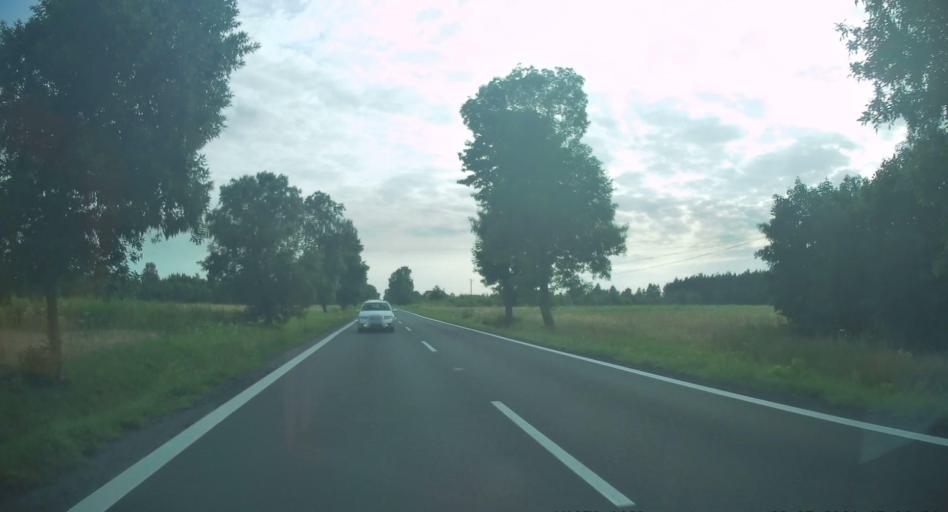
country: PL
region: Silesian Voivodeship
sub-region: Powiat czestochowski
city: Rudniki
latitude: 50.8961
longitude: 19.2782
